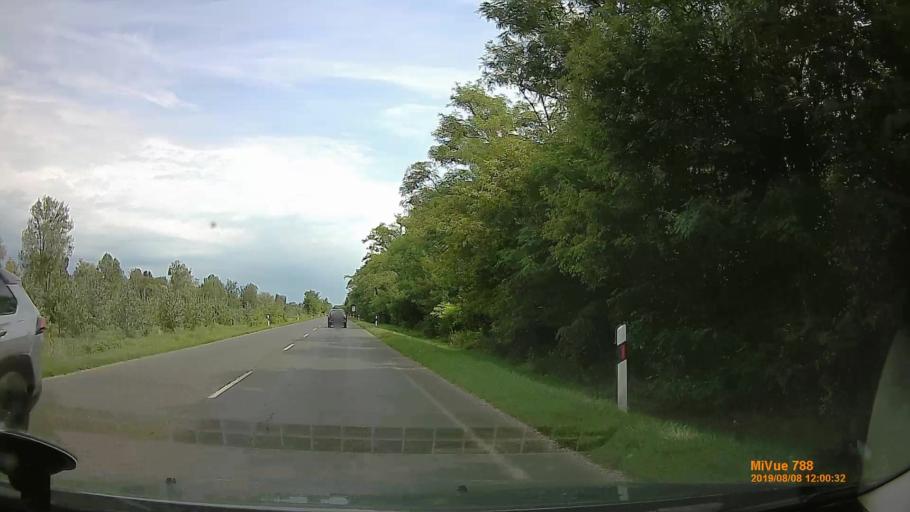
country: HU
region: Somogy
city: Balatonlelle
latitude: 46.7973
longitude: 17.7312
